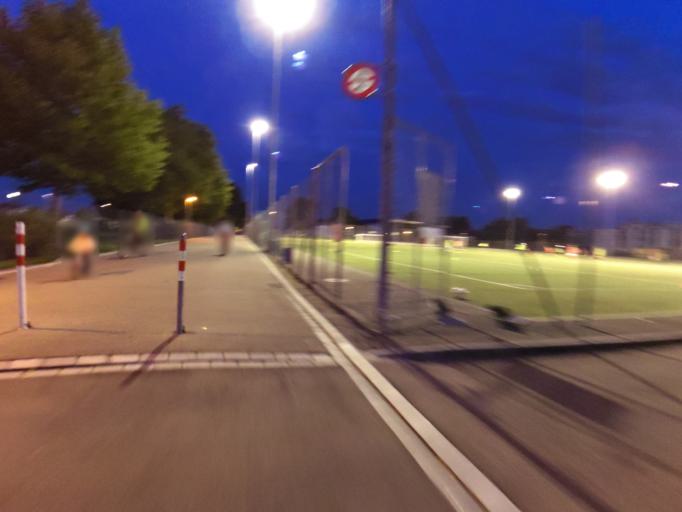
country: CH
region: Thurgau
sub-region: Frauenfeld District
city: Frauenfeld
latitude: 47.5633
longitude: 8.8871
